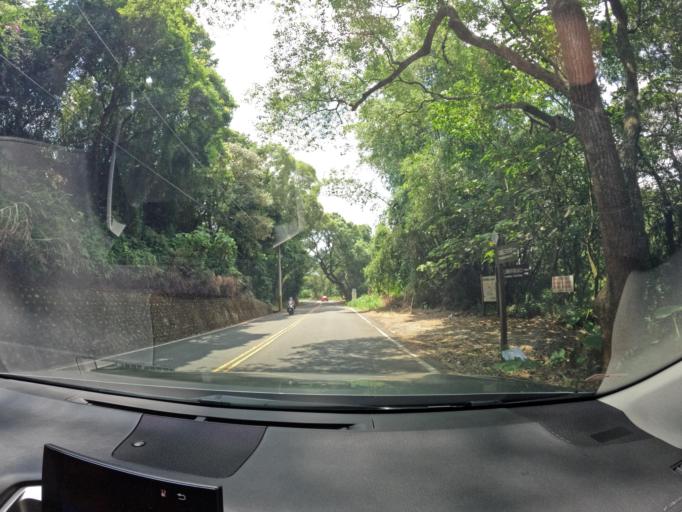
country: TW
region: Taiwan
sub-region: Nantou
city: Nantou
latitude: 23.8914
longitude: 120.6335
